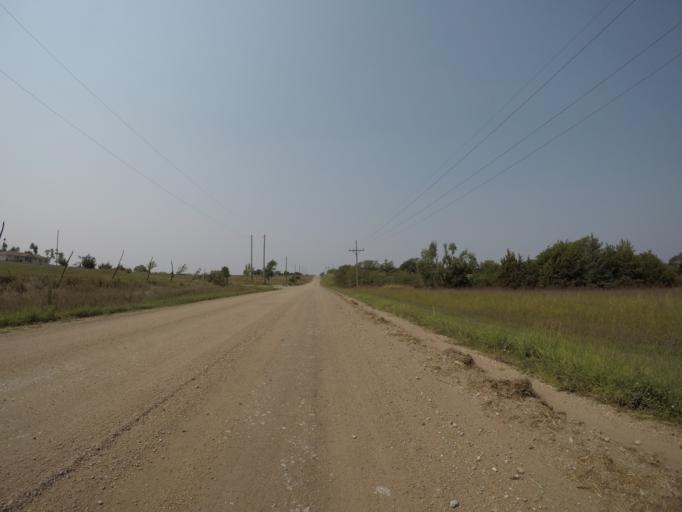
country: US
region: Nebraska
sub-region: Gage County
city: Beatrice
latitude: 40.2774
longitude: -96.7869
